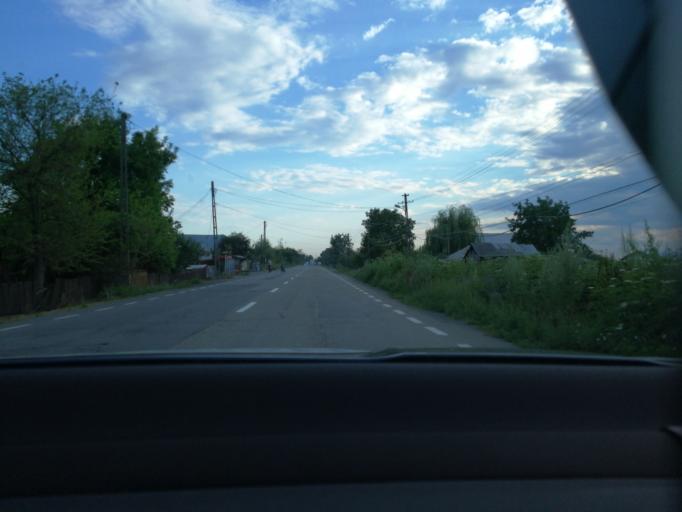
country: RO
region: Prahova
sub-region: Comuna Targsoru Vechi
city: Targsoru Vechi
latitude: 44.8738
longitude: 25.9386
